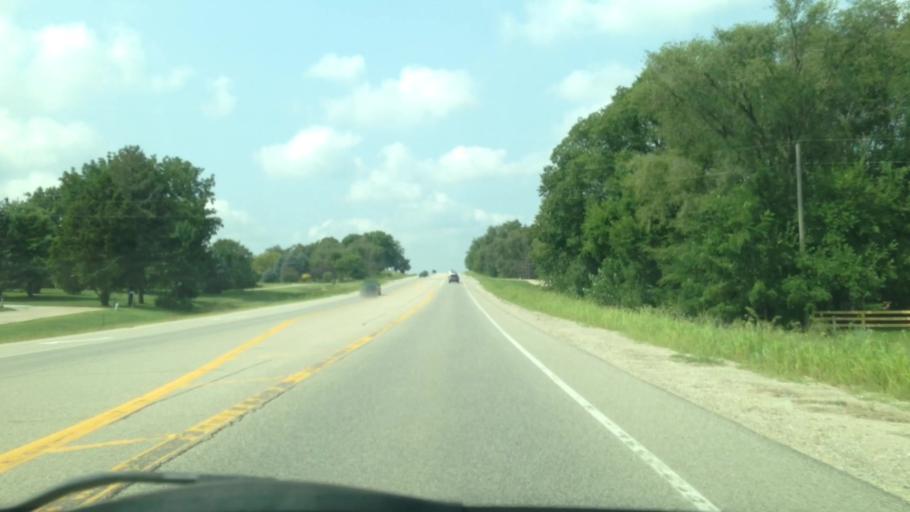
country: US
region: Iowa
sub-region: Linn County
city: Fairfax
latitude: 41.9375
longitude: -91.7594
